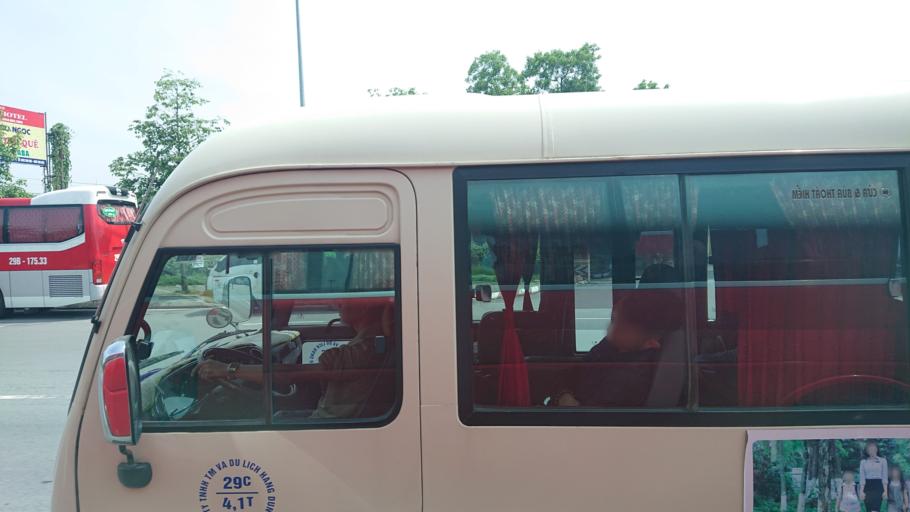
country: VN
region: Ha Noi
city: Soc Son
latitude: 21.2090
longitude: 105.8170
